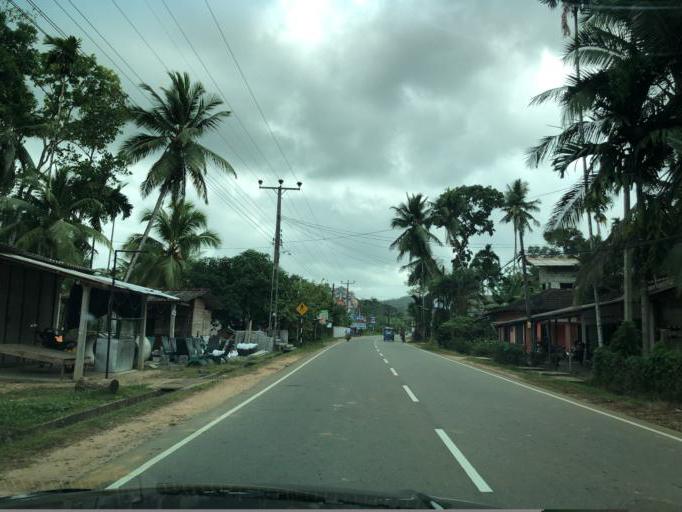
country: LK
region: Western
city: Horana South
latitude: 6.6789
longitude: 80.1603
